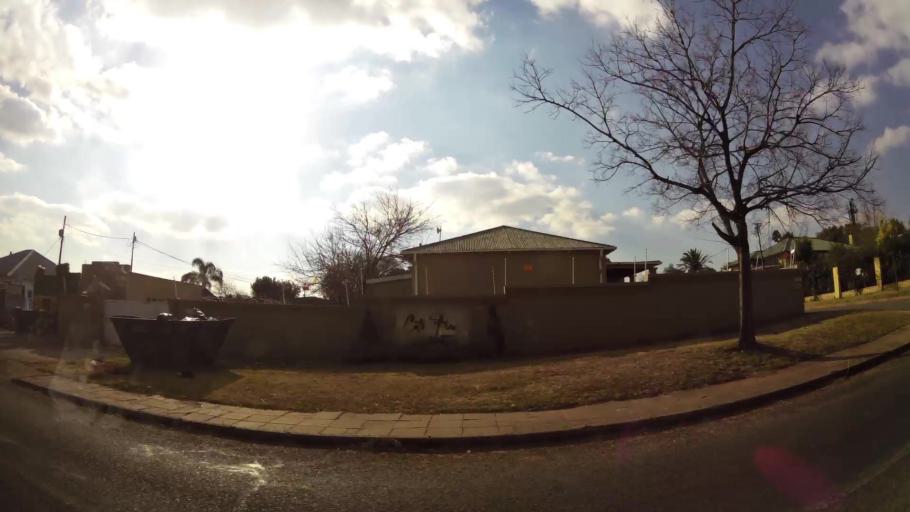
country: ZA
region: Gauteng
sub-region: West Rand District Municipality
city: Krugersdorp
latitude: -26.0880
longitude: 27.7687
